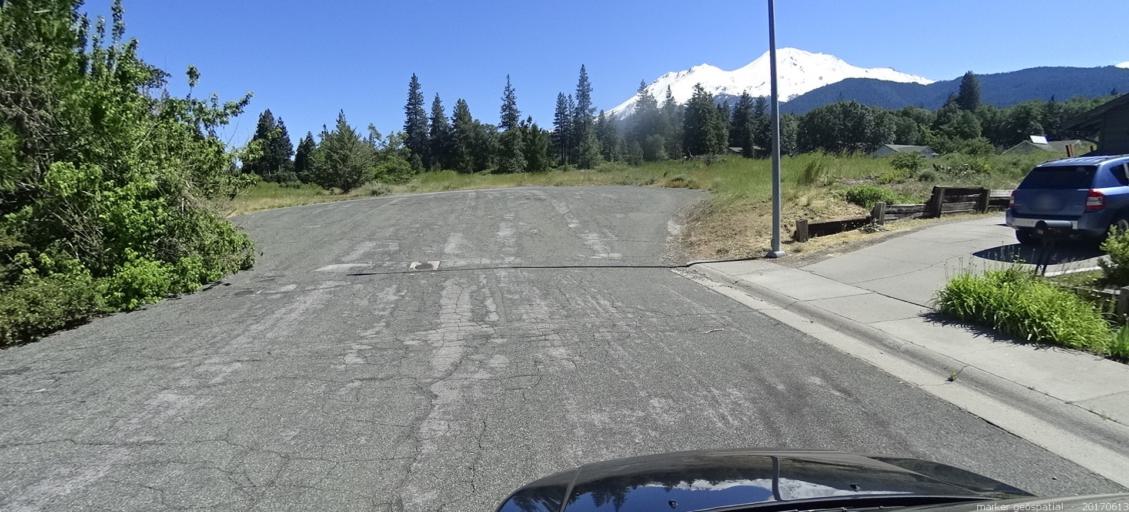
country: US
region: California
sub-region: Siskiyou County
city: Mount Shasta
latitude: 41.3215
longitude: -122.3153
